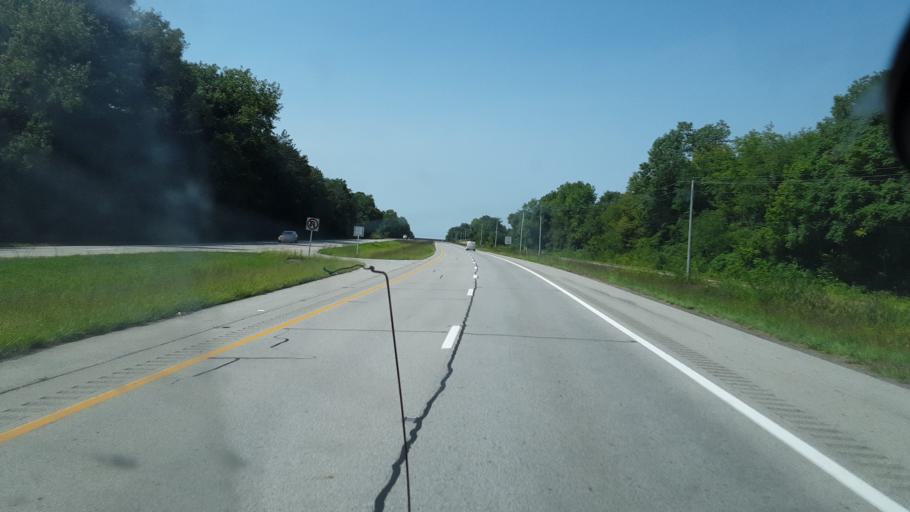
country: US
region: Ohio
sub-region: Muskingum County
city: Frazeysburg
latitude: 40.0788
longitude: -82.2396
